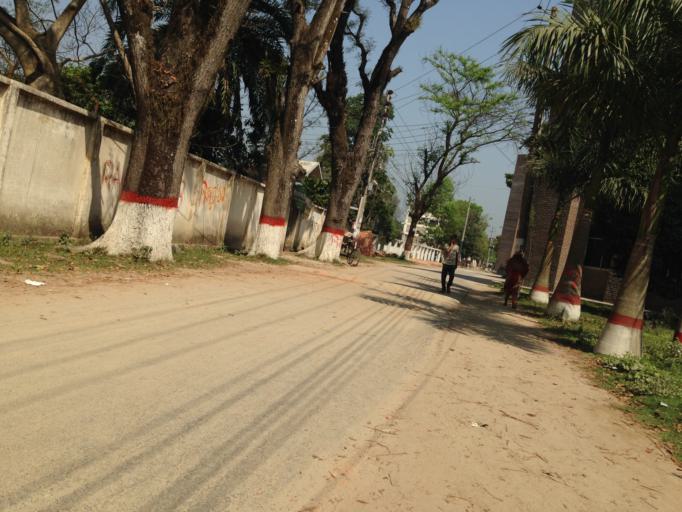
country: BD
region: Dhaka
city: Tangail
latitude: 24.2371
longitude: 89.8906
